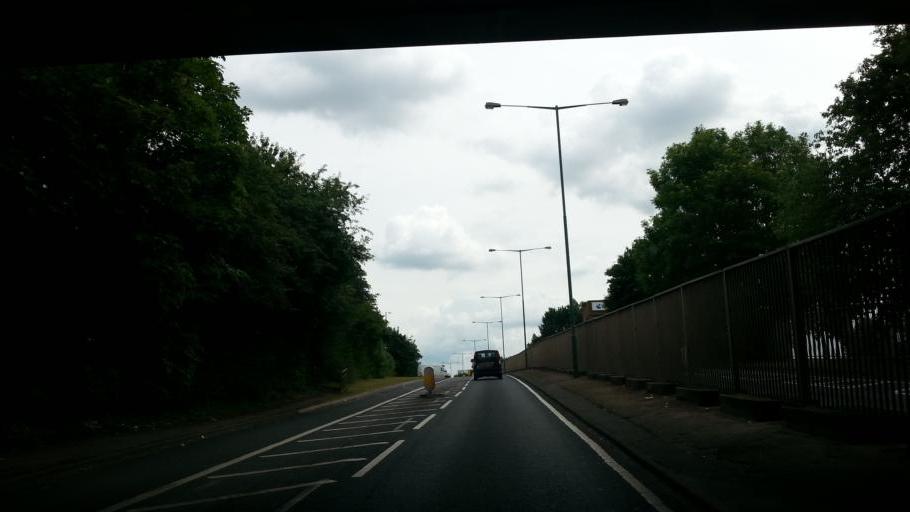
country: GB
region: England
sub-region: Solihull
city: Chelmsley Wood
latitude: 52.4826
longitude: -1.7299
